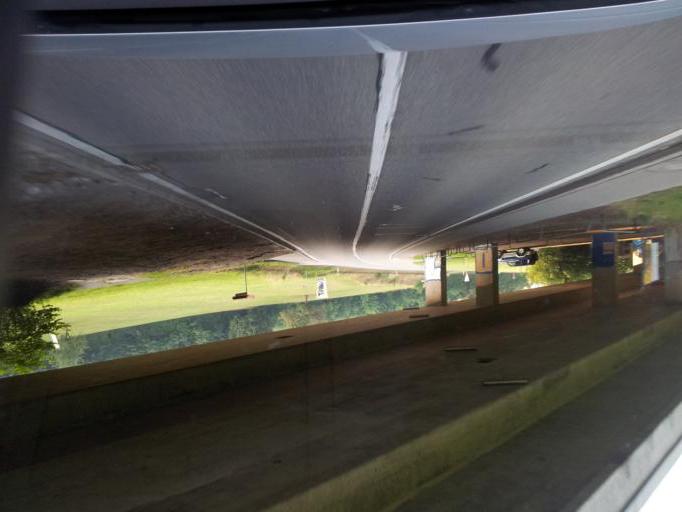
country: CH
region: Lucerne
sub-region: Sursee District
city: Schenkon
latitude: 47.1680
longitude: 8.1414
